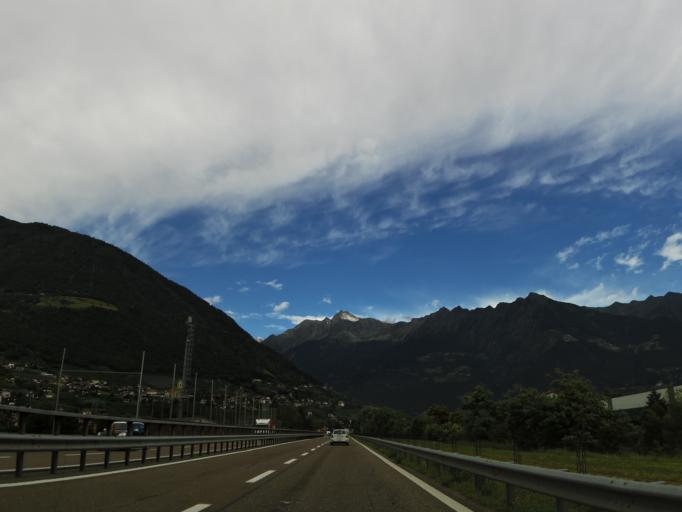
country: IT
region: Trentino-Alto Adige
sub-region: Bolzano
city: Marlengo
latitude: 46.6499
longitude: 11.1548
